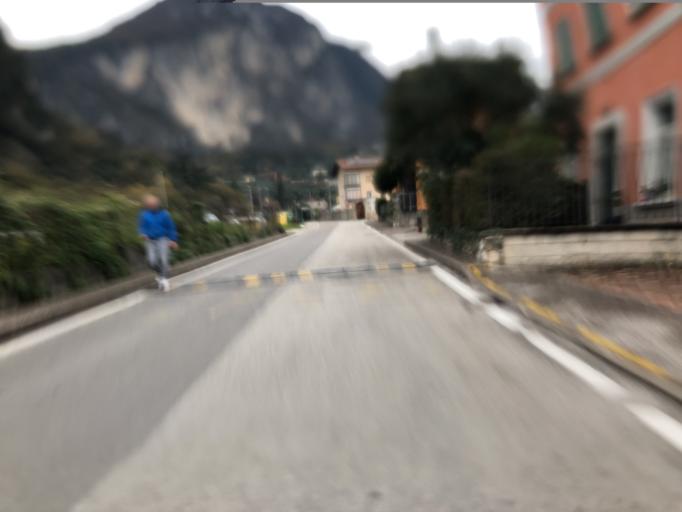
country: IT
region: Trentino-Alto Adige
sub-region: Provincia di Trento
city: Riva del Garda
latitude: 45.8923
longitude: 10.8380
